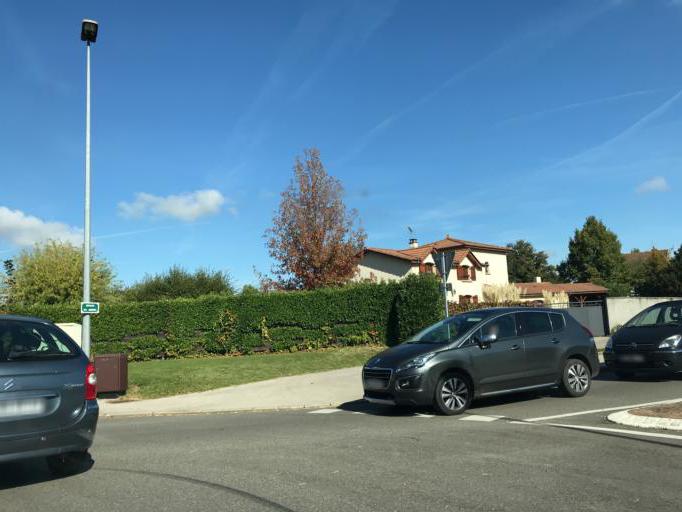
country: FR
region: Rhone-Alpes
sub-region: Departement de l'Ain
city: Saint-Didier-sur-Chalaronne
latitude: 46.1792
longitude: 4.8197
